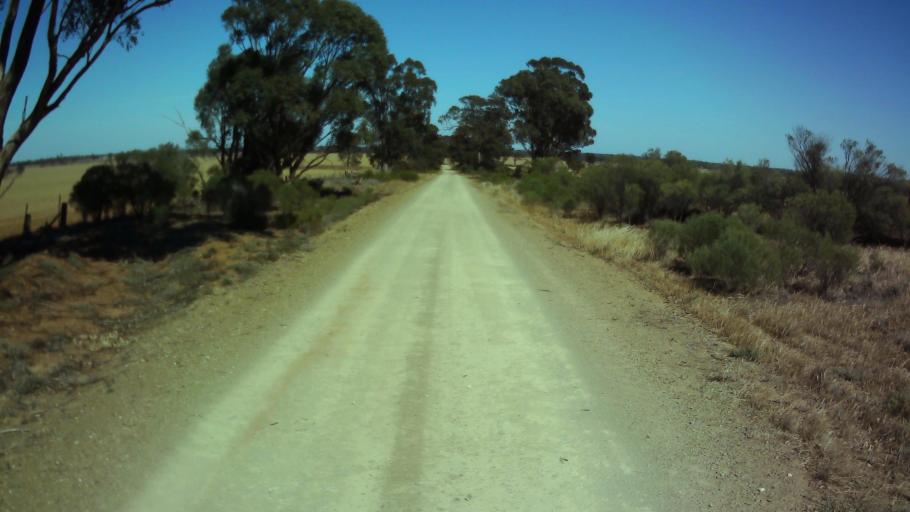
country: AU
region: New South Wales
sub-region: Weddin
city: Grenfell
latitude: -33.8799
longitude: 147.8808
